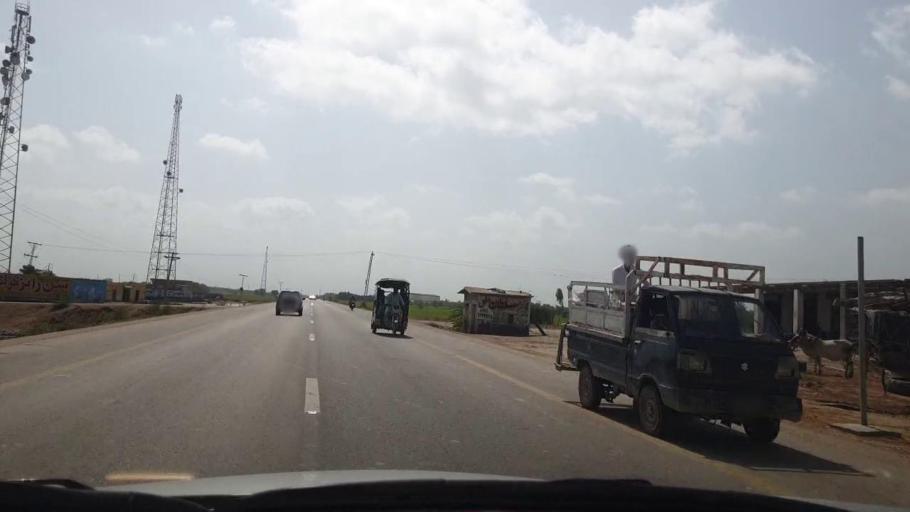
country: PK
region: Sindh
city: Matli
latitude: 24.9409
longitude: 68.7036
